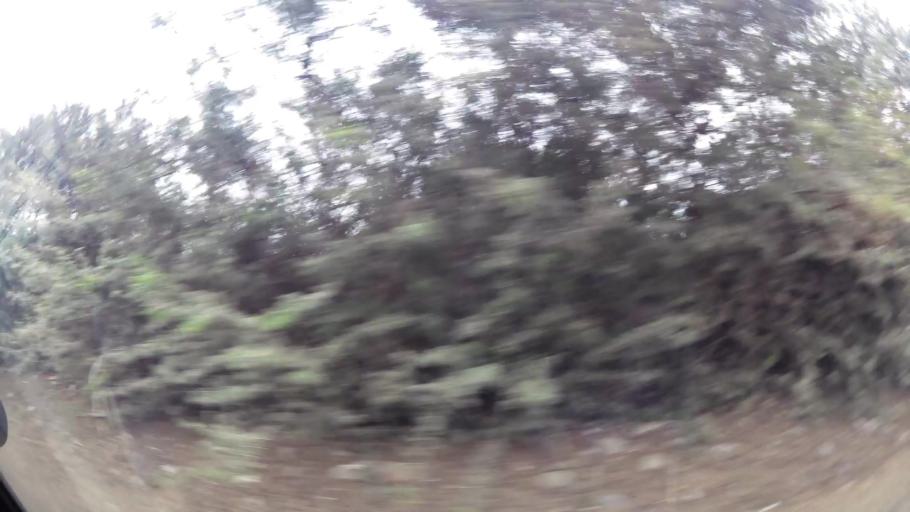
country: PE
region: Ica
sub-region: Provincia de Pisco
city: Pisco
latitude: -13.7409
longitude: -76.1954
